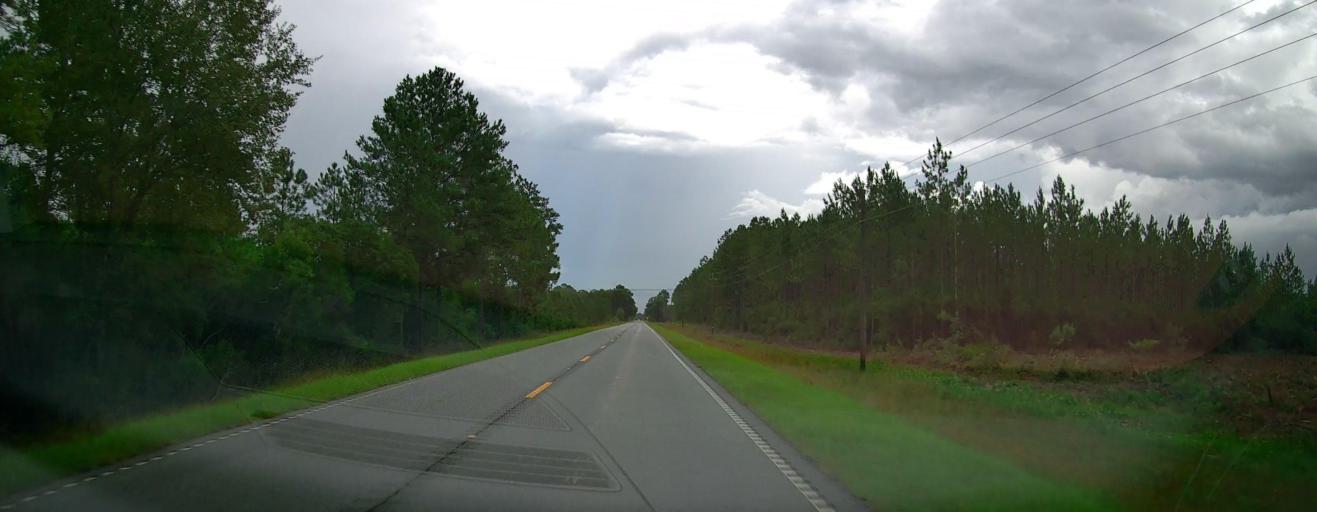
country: US
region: Georgia
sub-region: Pierce County
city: Blackshear
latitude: 31.3633
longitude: -82.0789
